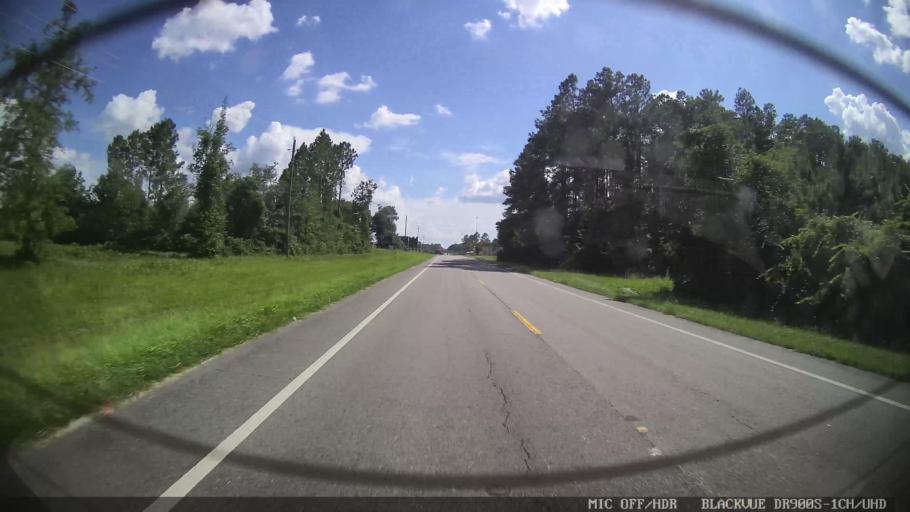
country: US
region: Florida
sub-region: Hamilton County
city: Jasper
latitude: 30.5300
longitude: -83.0484
